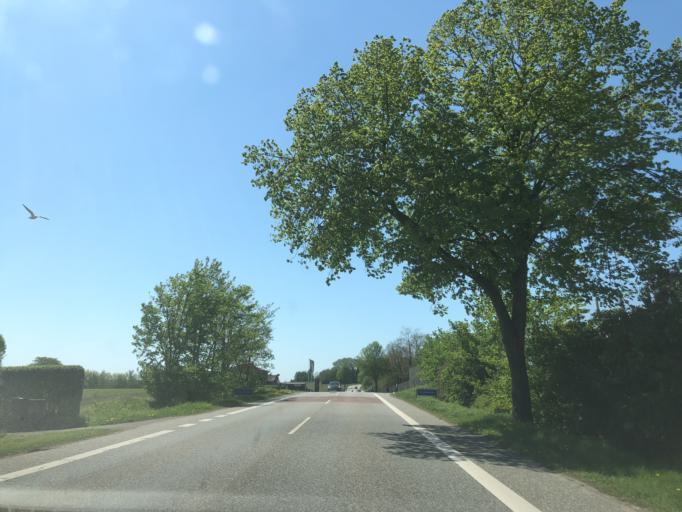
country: DK
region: Zealand
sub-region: Slagelse Kommune
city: Forlev
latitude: 55.3635
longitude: 11.2681
